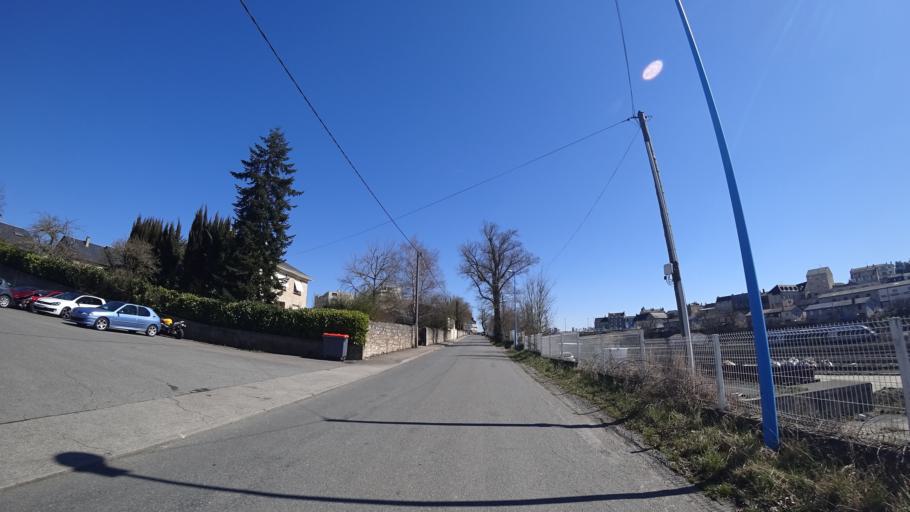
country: FR
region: Midi-Pyrenees
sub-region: Departement de l'Aveyron
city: Rodez
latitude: 44.3633
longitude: 2.5846
